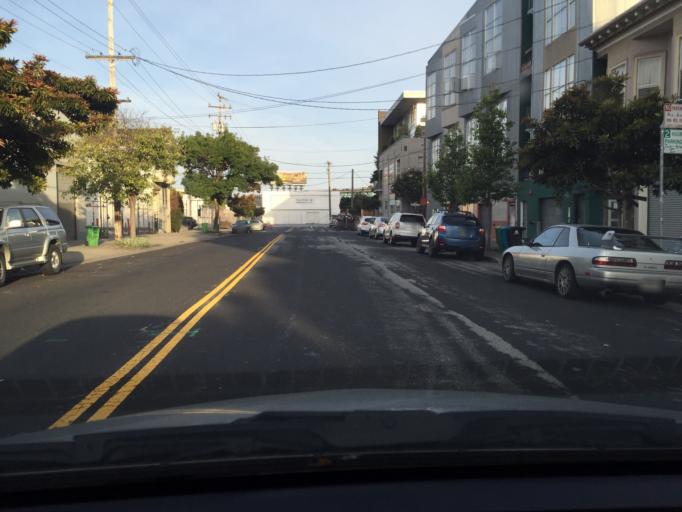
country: US
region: California
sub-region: San Francisco County
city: San Francisco
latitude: 37.7707
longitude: -122.4145
